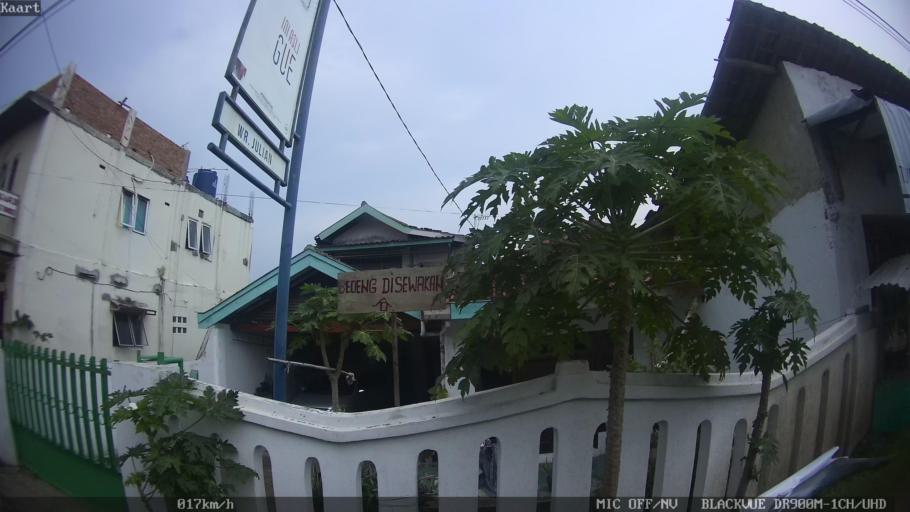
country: ID
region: Lampung
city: Bandarlampung
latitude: -5.4221
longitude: 105.2759
